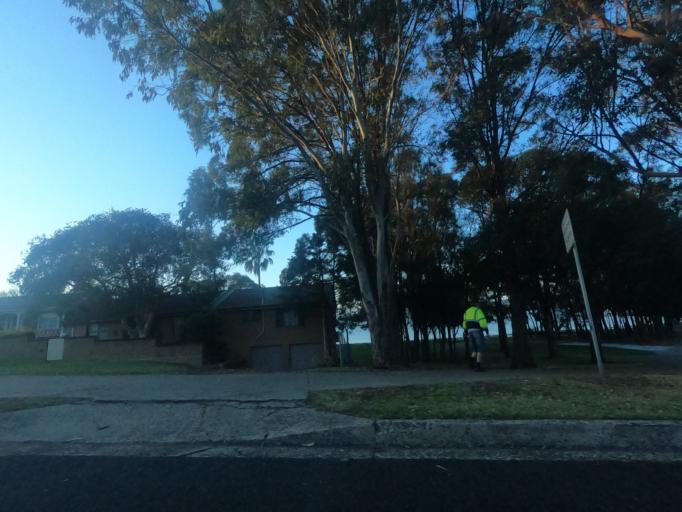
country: AU
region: New South Wales
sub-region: Wollongong
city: Koonawarra
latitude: -34.5001
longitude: 150.8203
